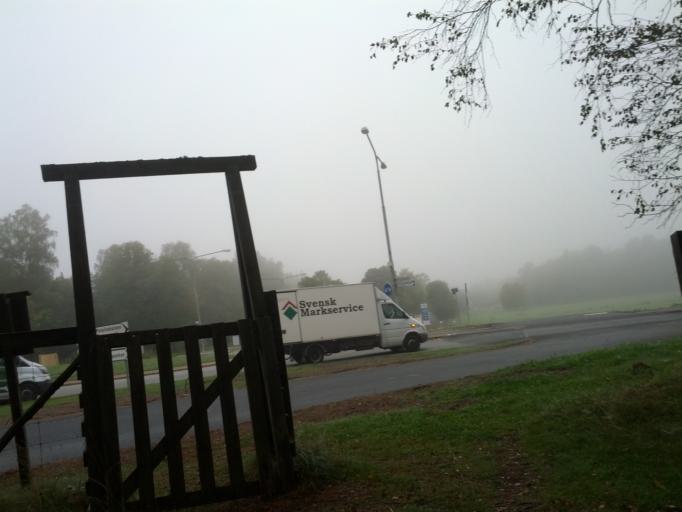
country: SE
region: Uppsala
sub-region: Uppsala Kommun
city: Uppsala
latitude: 59.8389
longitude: 17.6408
